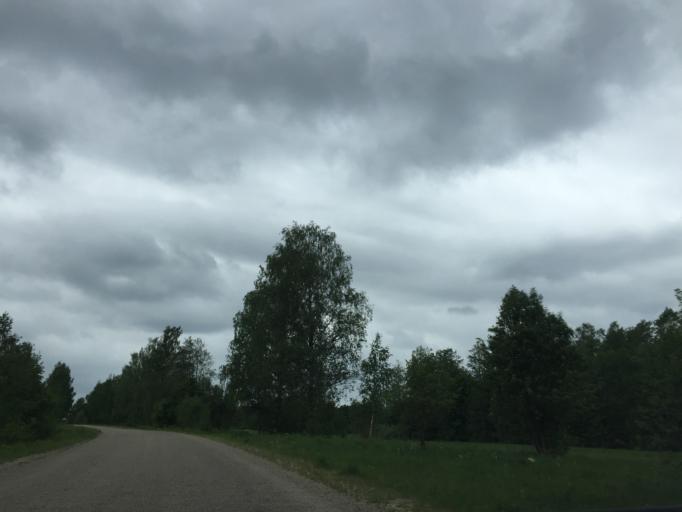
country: LV
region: Aglona
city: Aglona
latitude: 56.0846
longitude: 26.9220
